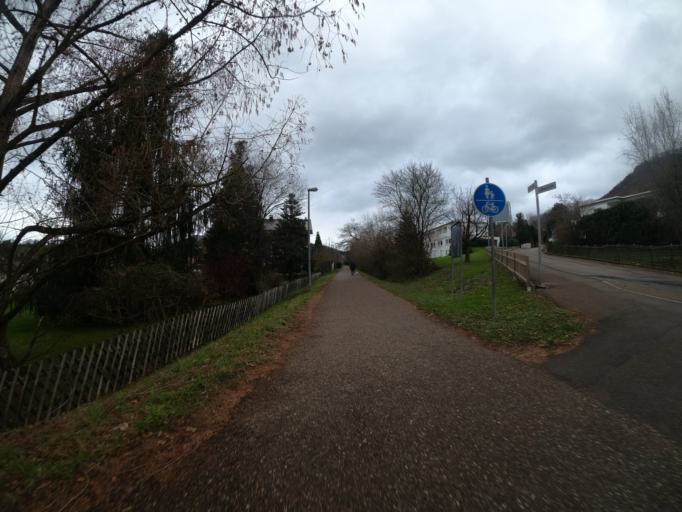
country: DE
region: Baden-Wuerttemberg
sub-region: Regierungsbezirk Stuttgart
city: Donzdorf
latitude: 48.6871
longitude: 9.8159
